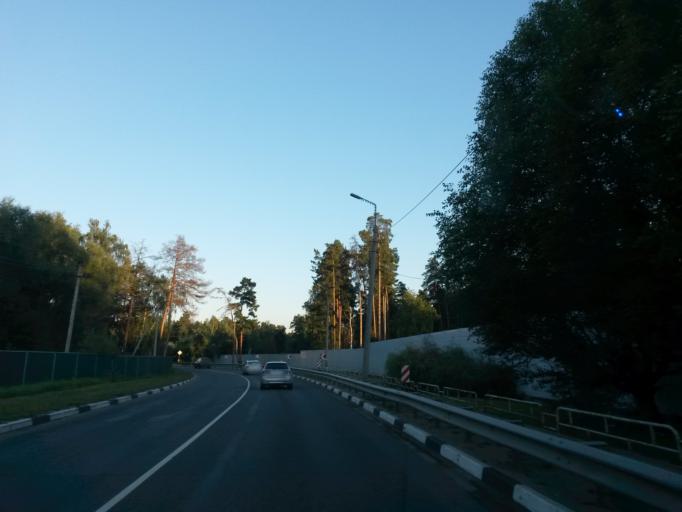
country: RU
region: Moskovskaya
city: Domodedovo
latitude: 55.3589
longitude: 37.7222
